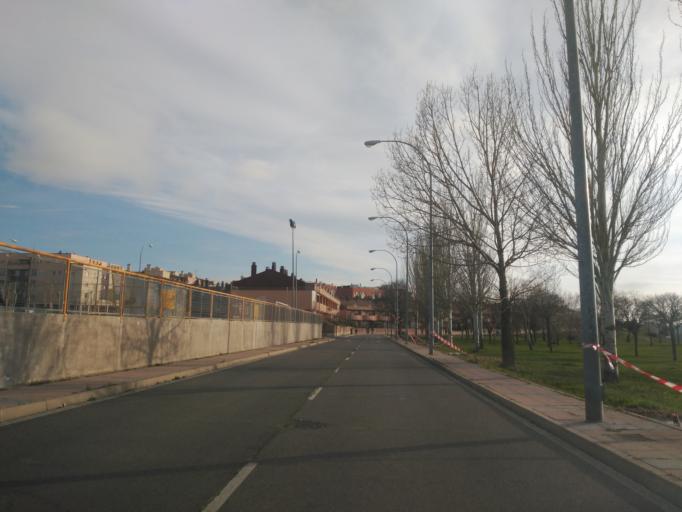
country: ES
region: Castille and Leon
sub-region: Provincia de Salamanca
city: Salamanca
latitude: 40.9496
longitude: -5.6733
